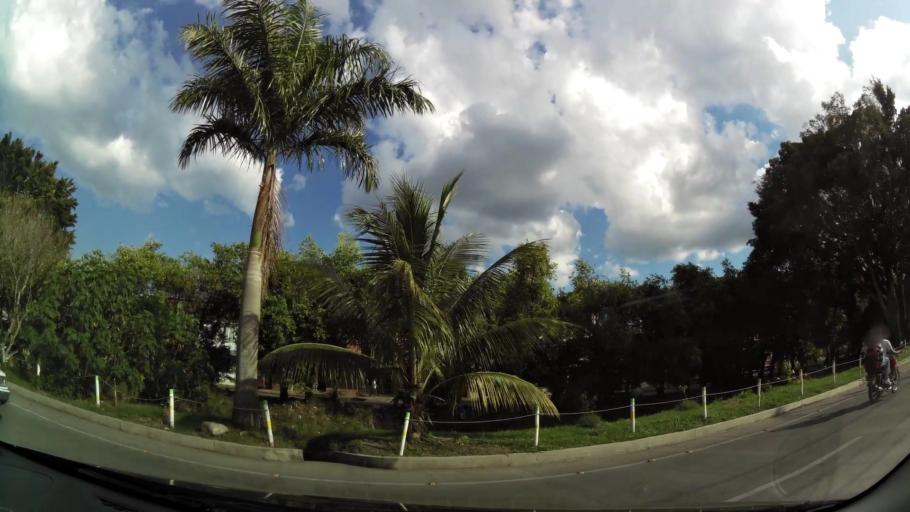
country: CO
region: Valle del Cauca
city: Cali
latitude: 3.4034
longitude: -76.5095
